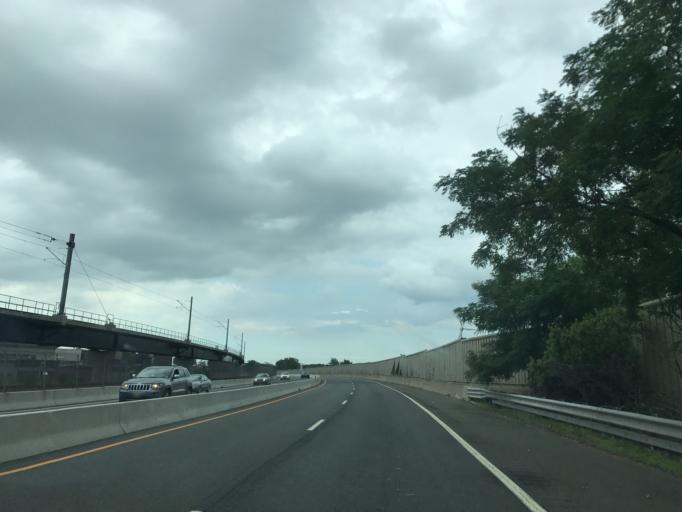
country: US
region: New Jersey
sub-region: Hudson County
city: Bayonne
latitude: 40.6540
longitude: -74.1281
